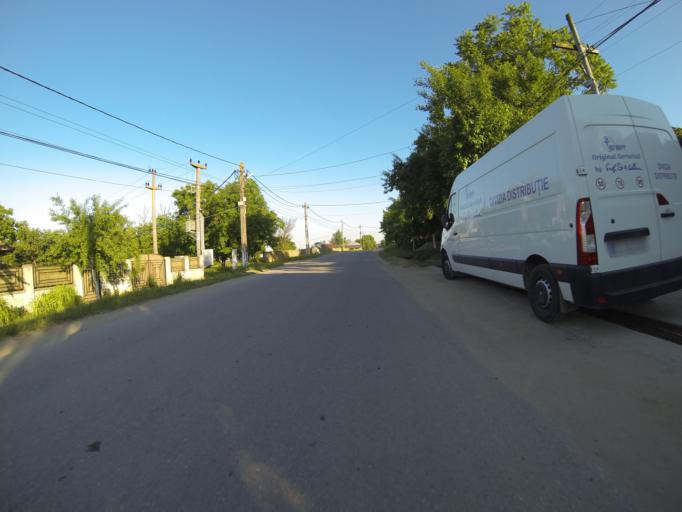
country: RO
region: Dolj
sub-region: Comuna Tuglui
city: Tuglui
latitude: 44.2075
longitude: 23.7959
